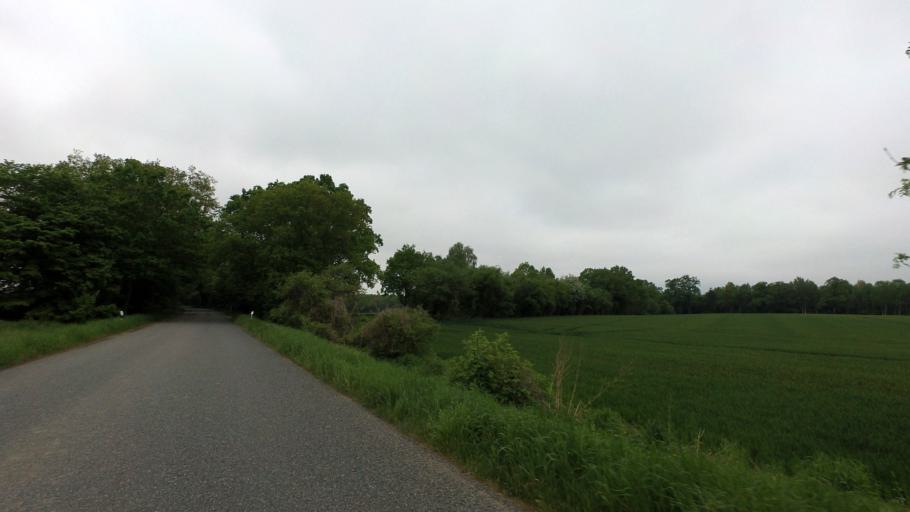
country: DE
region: Mecklenburg-Vorpommern
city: Mollenhagen
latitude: 53.6100
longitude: 12.9207
